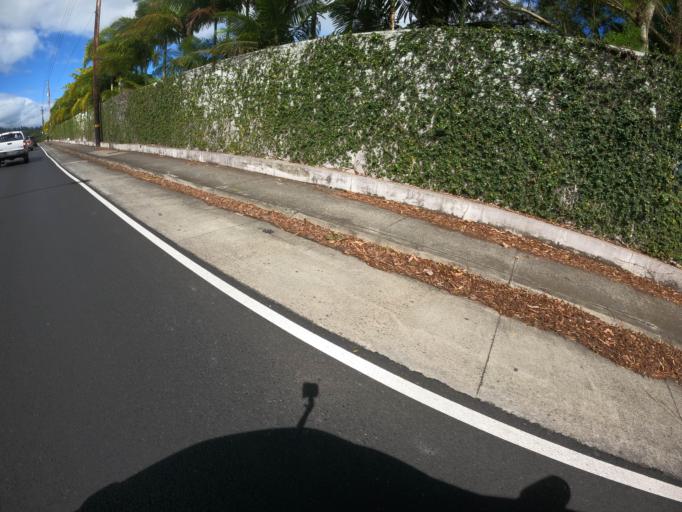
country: US
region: Hawaii
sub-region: Honolulu County
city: He'eia
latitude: 21.4155
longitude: -157.8122
